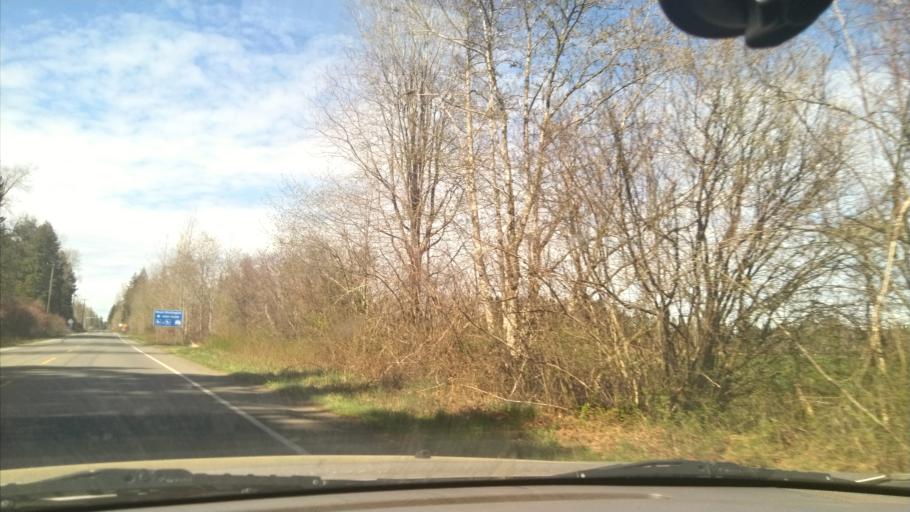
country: CA
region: British Columbia
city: Courtenay
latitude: 49.7038
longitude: -125.0220
